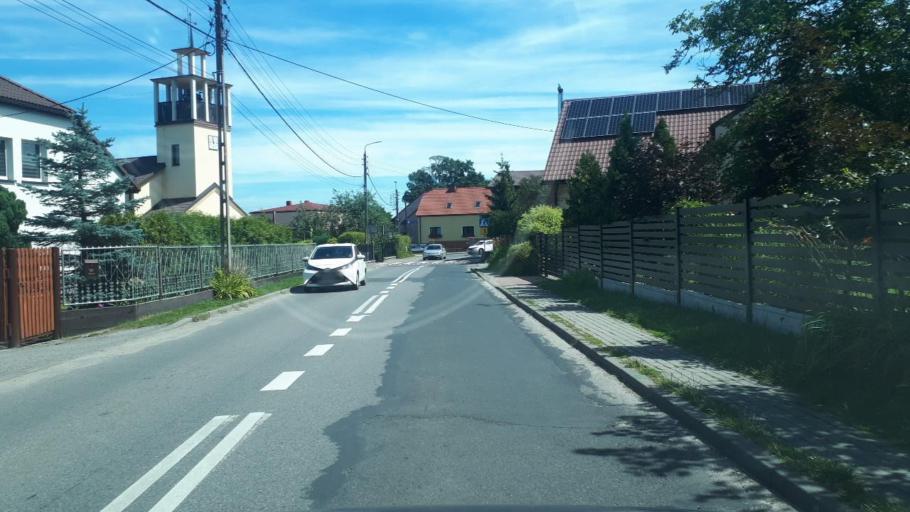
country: PL
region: Silesian Voivodeship
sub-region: Tychy
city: Cielmice
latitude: 50.0899
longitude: 19.0163
